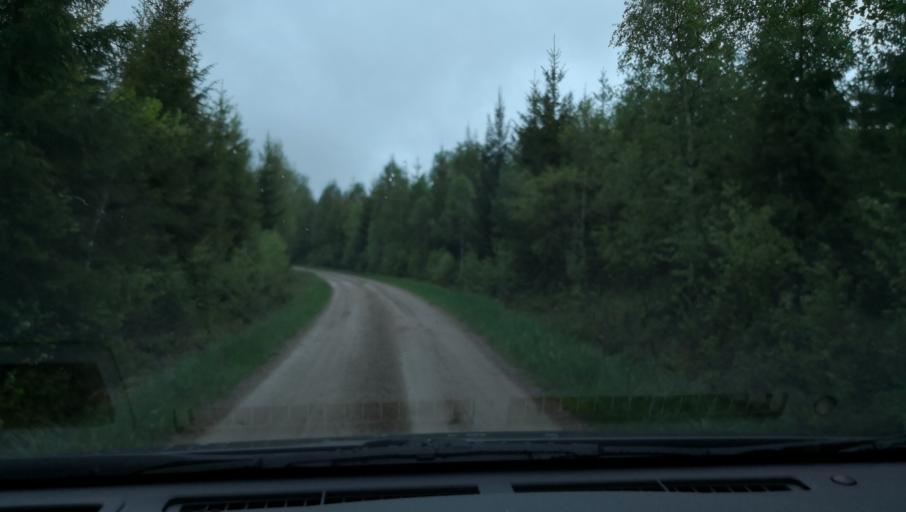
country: SE
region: Uppsala
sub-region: Enkopings Kommun
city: Orsundsbro
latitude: 59.9228
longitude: 17.3412
